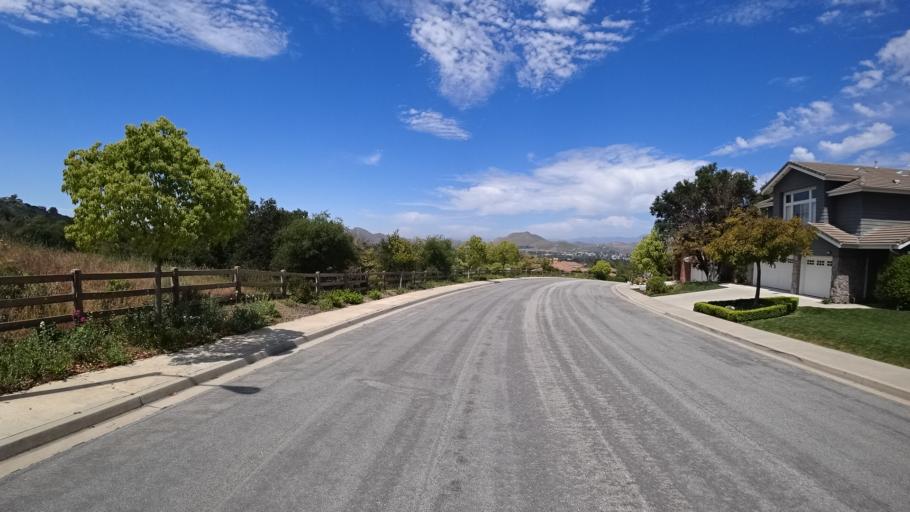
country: US
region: California
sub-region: Ventura County
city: Casa Conejo
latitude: 34.1731
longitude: -118.9184
